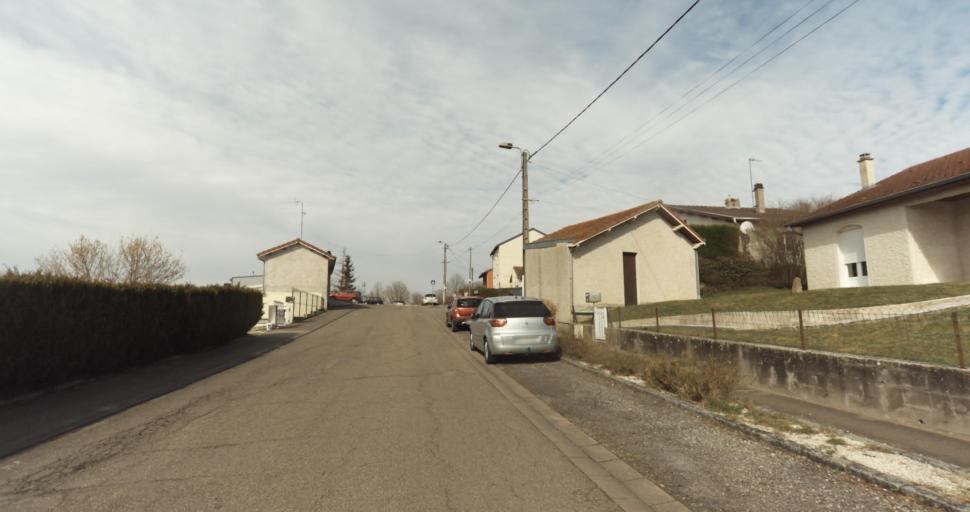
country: FR
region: Lorraine
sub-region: Departement de Meurthe-et-Moselle
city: Jarny
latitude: 49.1603
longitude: 5.8684
